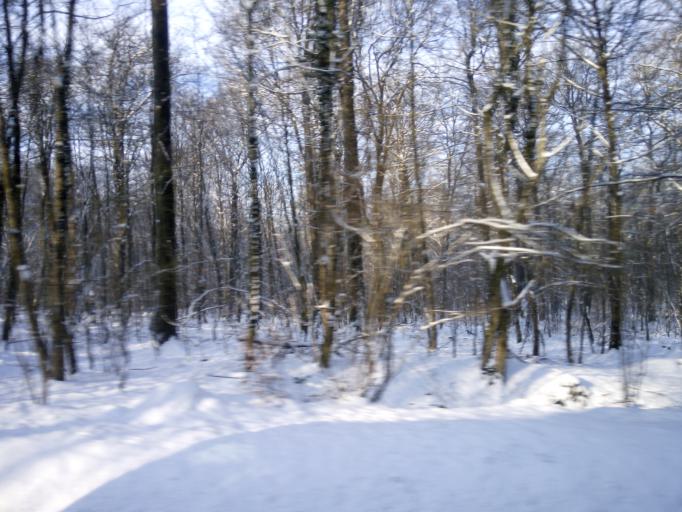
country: LU
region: Grevenmacher
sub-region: Canton d'Echternach
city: Berdorf
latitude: 49.8073
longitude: 6.3404
